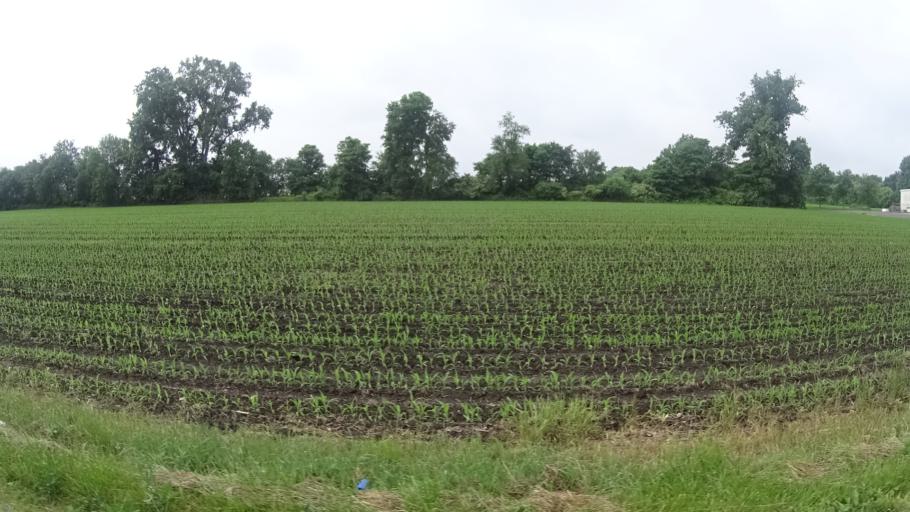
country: US
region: Ohio
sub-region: Erie County
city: Sandusky
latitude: 41.3603
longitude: -82.7475
